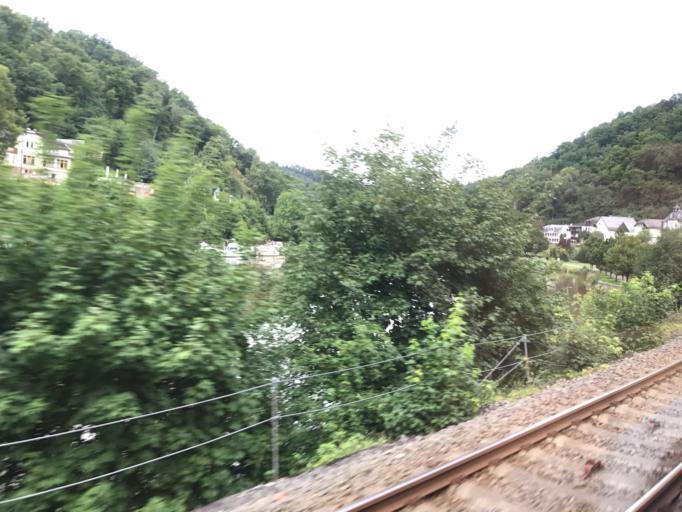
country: DE
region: Rheinland-Pfalz
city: Balduinstein
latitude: 50.3436
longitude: 7.9687
